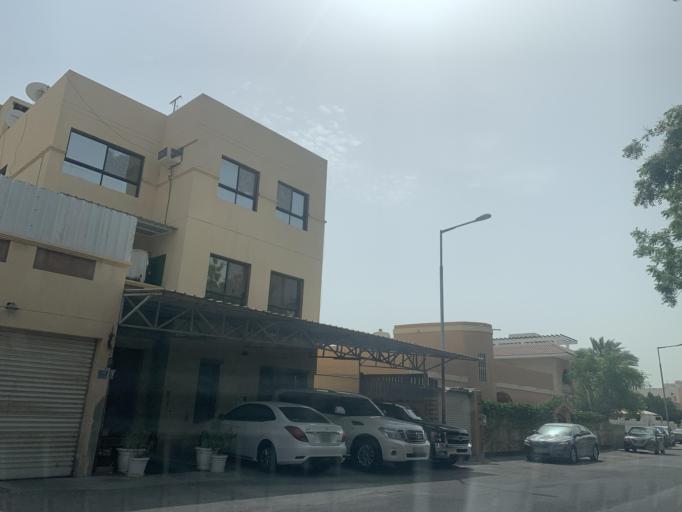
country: BH
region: Northern
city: Ar Rifa'
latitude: 26.1336
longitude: 50.5704
